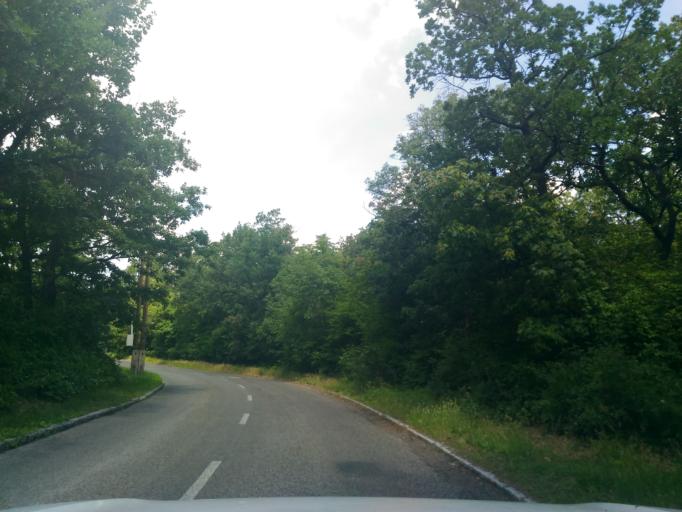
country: HU
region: Baranya
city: Pecs
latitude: 46.0916
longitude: 18.2292
